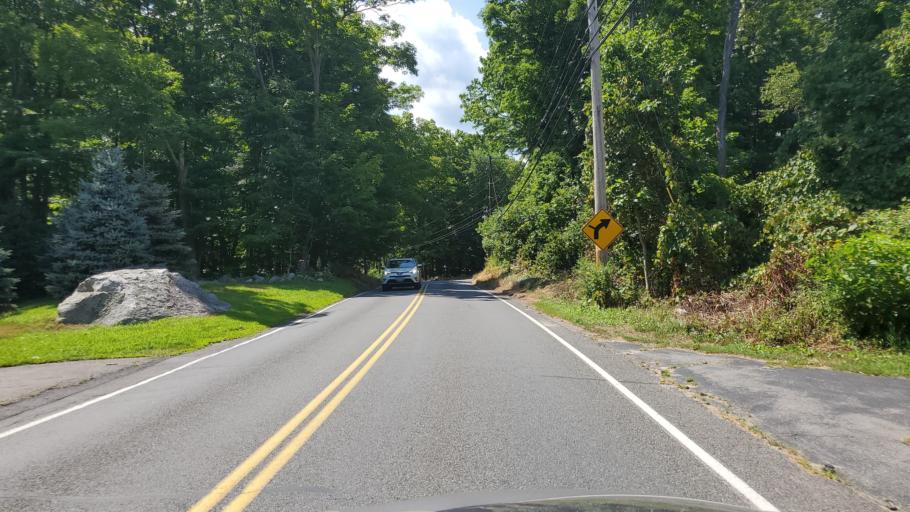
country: US
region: Connecticut
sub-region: Fairfield County
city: Newtown
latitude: 41.3232
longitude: -73.2780
